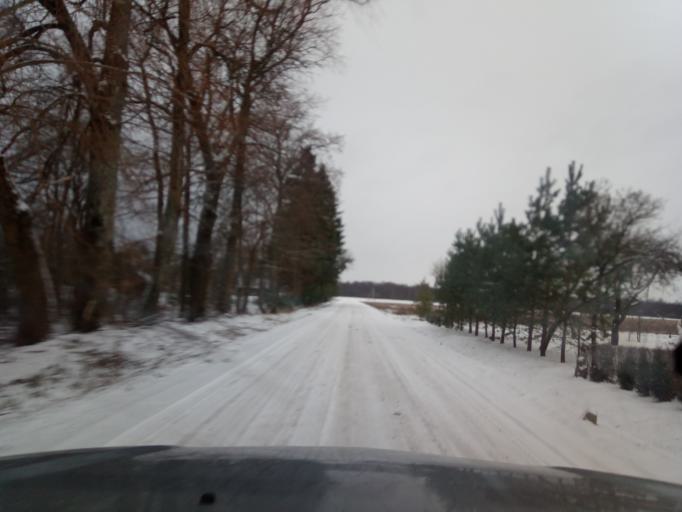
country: LT
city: Ramygala
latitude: 55.4836
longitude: 24.5723
